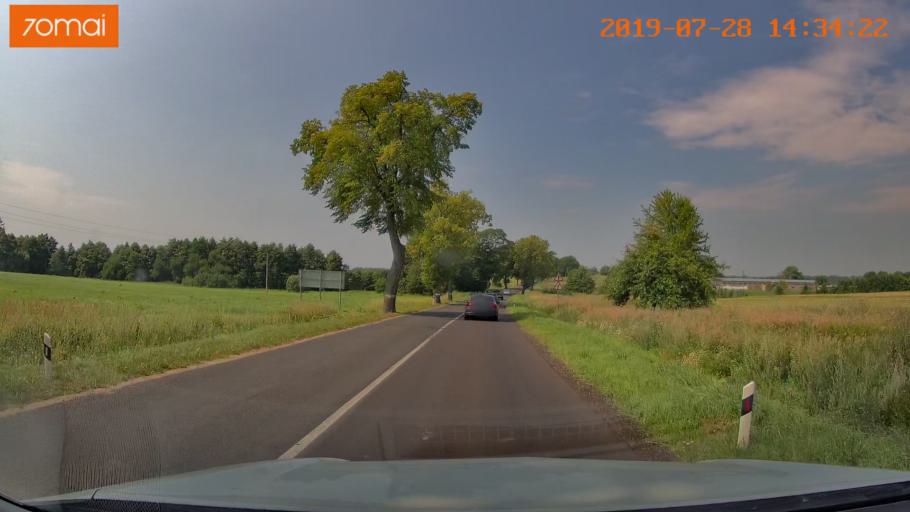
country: RU
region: Kaliningrad
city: Primorsk
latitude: 54.8249
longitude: 20.0194
